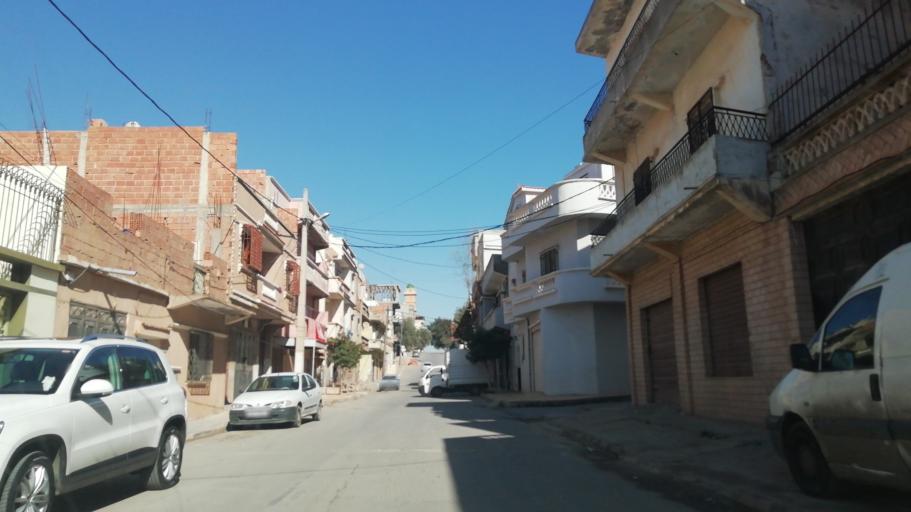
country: DZ
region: Oran
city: Bir el Djir
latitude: 35.7250
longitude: -0.5807
